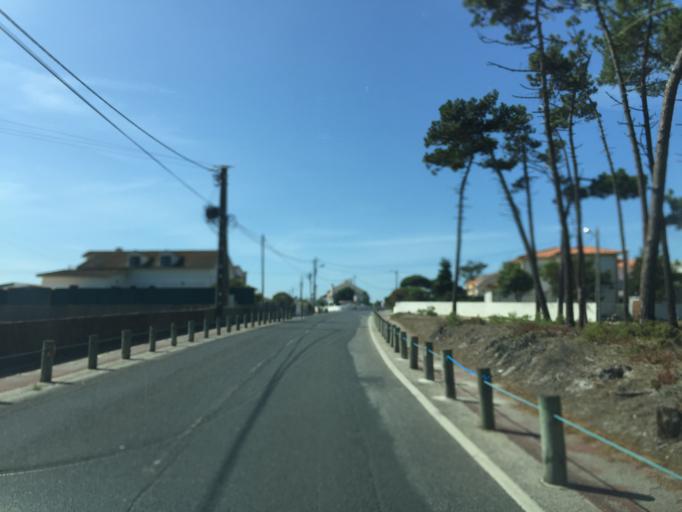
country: PT
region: Lisbon
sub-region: Torres Vedras
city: Silveira
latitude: 39.1538
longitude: -9.3609
